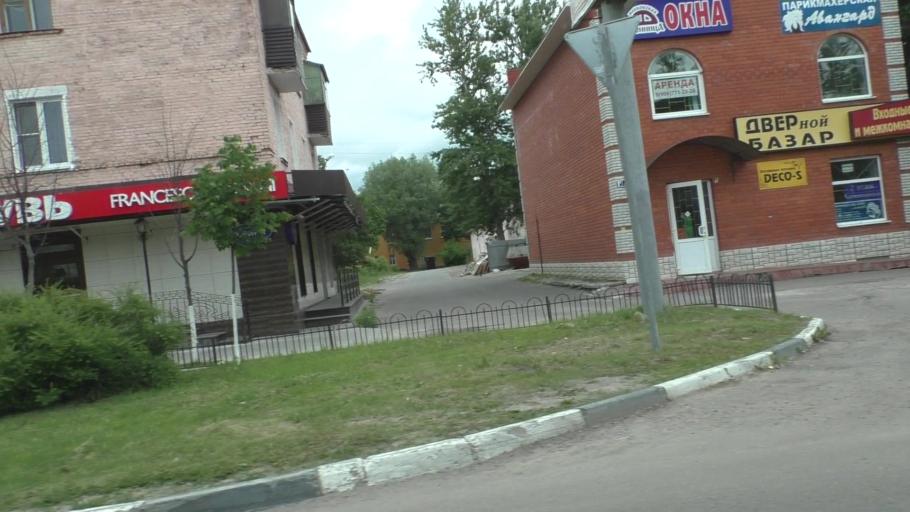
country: RU
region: Moskovskaya
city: Yegor'yevsk
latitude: 55.3734
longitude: 39.0524
